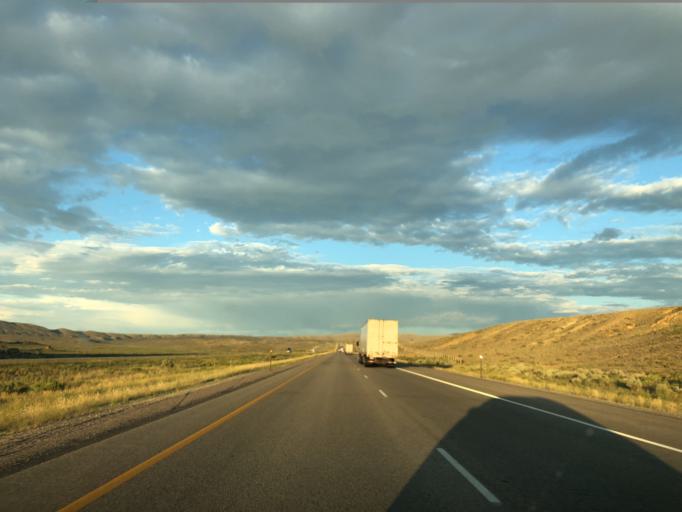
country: US
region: Wyoming
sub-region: Carbon County
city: Saratoga
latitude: 41.7345
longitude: -106.7337
